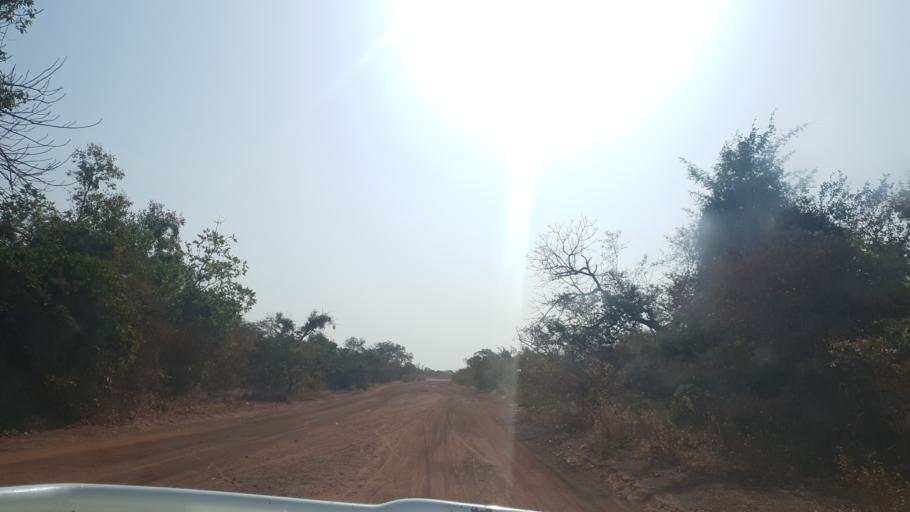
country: ML
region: Koulikoro
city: Dioila
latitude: 12.6943
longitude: -6.7537
